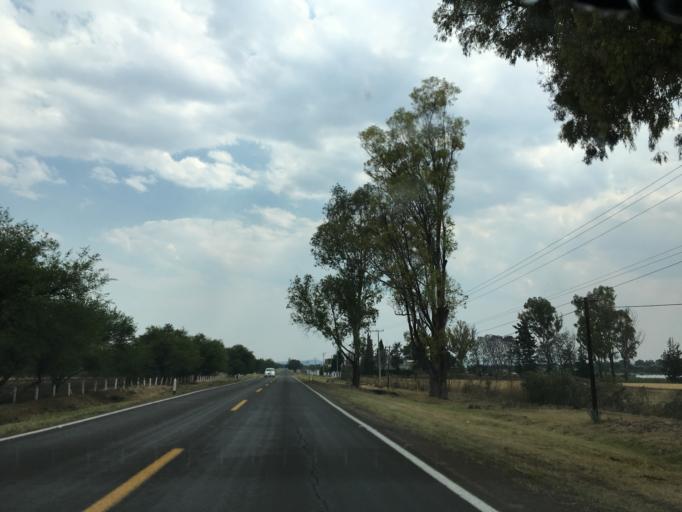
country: MX
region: Michoacan
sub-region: Cuitzeo
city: Cuamio
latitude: 20.0131
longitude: -101.1546
